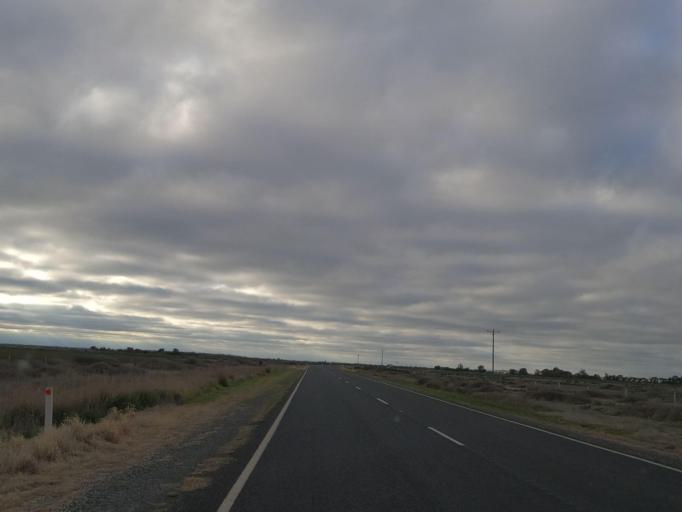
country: AU
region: Victoria
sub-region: Swan Hill
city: Swan Hill
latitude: -35.8450
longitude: 143.9382
